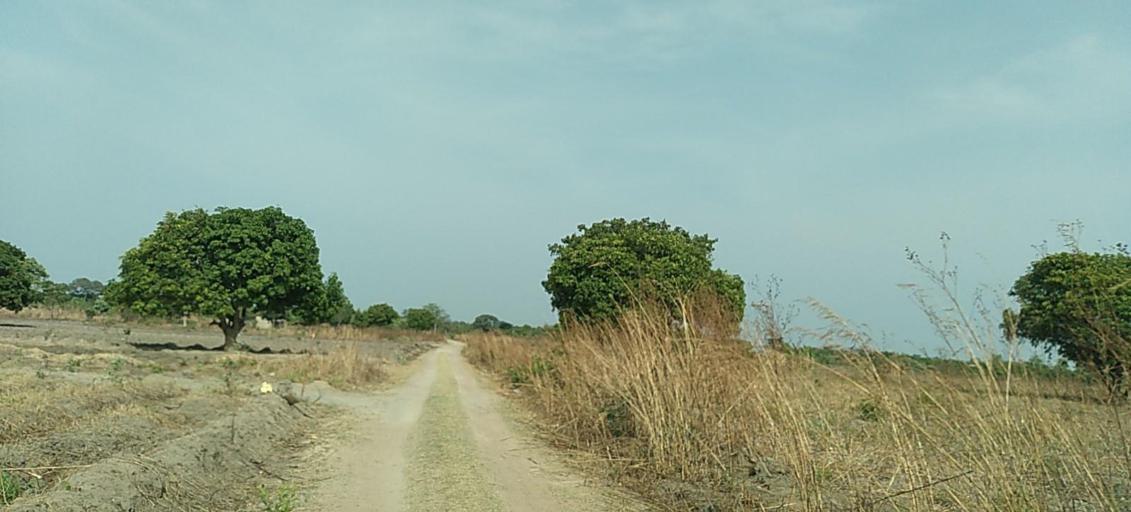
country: ZM
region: Copperbelt
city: Luanshya
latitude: -13.2177
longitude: 28.6520
